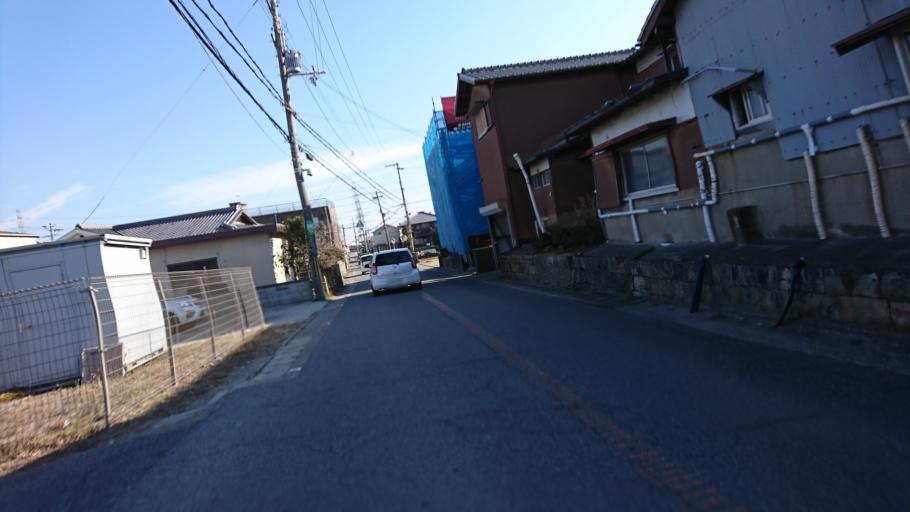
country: JP
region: Hyogo
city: Kakogawacho-honmachi
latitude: 34.8120
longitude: 134.8520
